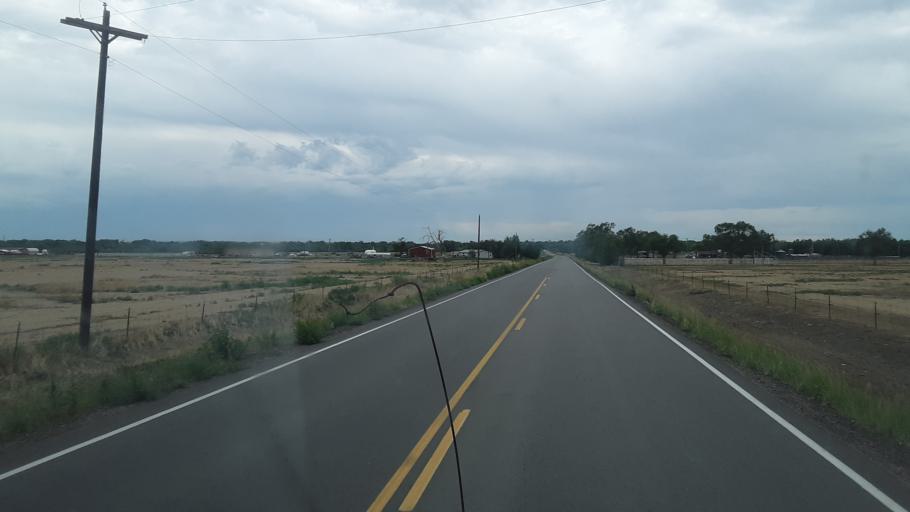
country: US
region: Colorado
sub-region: Otero County
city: Fowler
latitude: 38.1524
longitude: -104.0232
